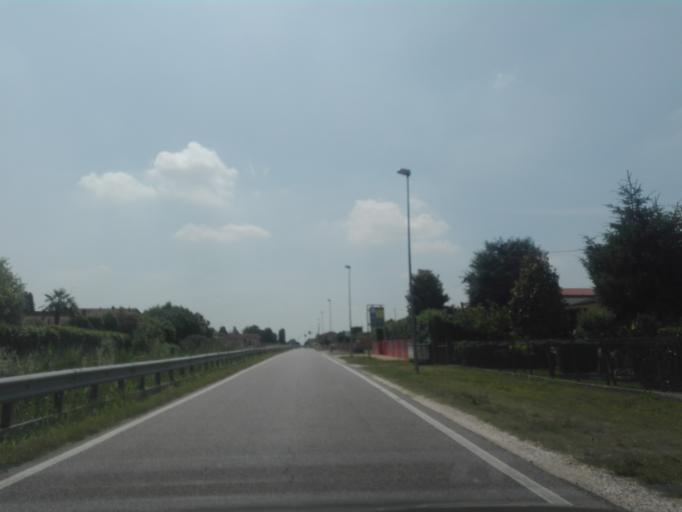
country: IT
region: Veneto
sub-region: Provincia di Rovigo
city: Grignano Polesine
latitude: 45.0463
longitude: 11.7444
